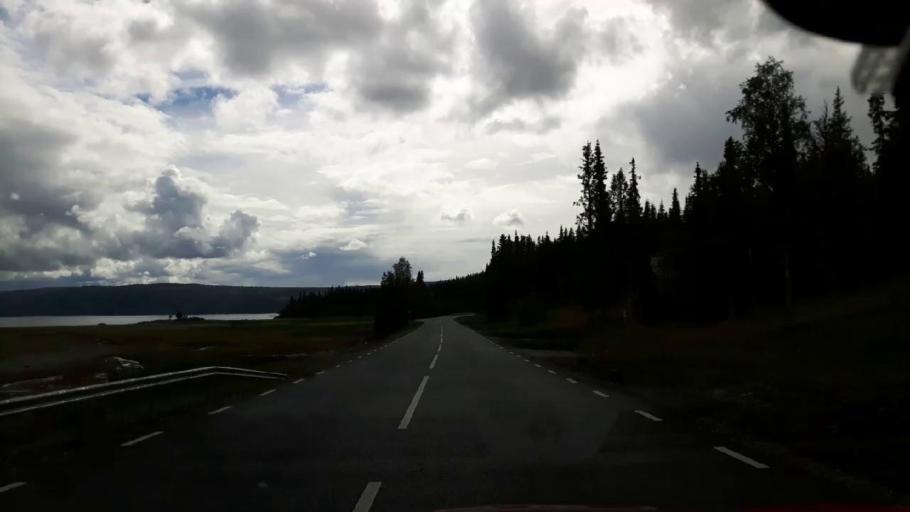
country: NO
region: Nord-Trondelag
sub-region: Royrvik
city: Royrvik
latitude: 64.8198
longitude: 14.0608
